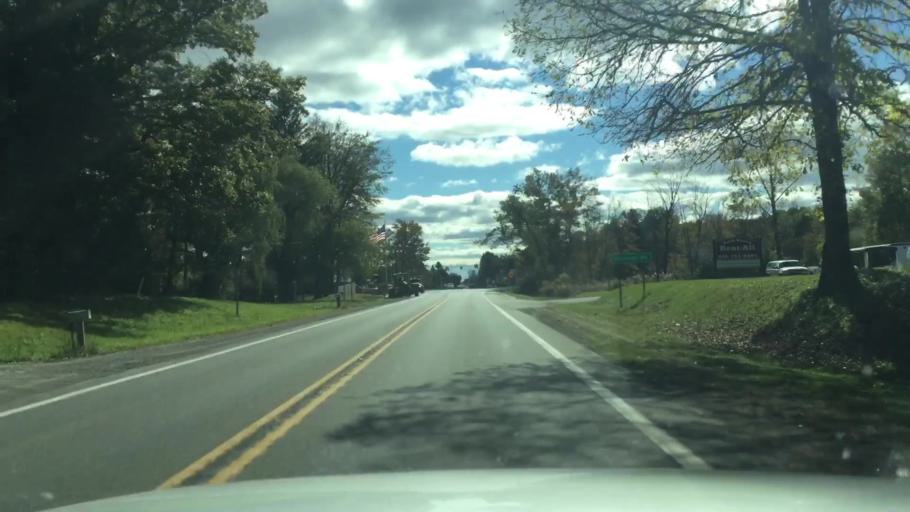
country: US
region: Michigan
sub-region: Lapeer County
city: Barnes Lake-Millers Lake
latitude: 43.2072
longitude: -83.3131
